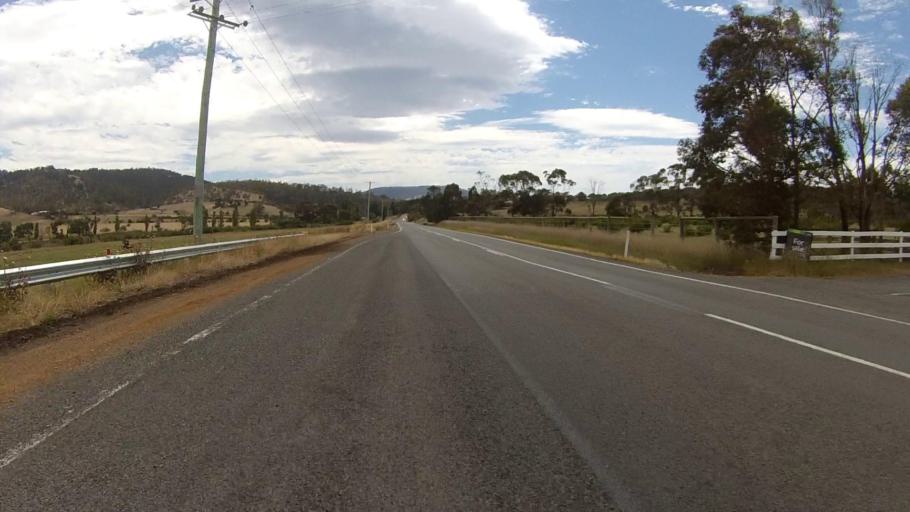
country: AU
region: Tasmania
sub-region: Brighton
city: Old Beach
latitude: -42.6753
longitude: 147.3581
